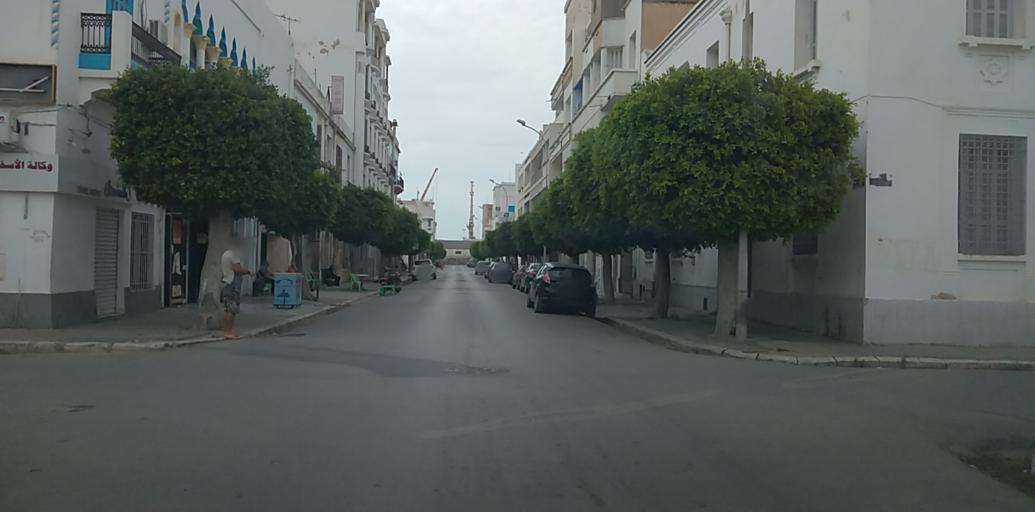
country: TN
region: Safaqis
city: Sfax
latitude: 34.7331
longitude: 10.7658
